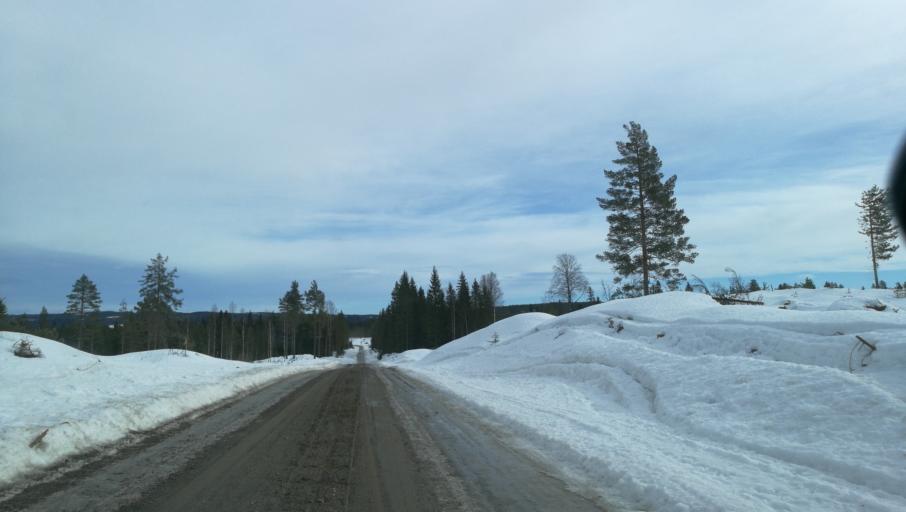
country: SE
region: Vaermland
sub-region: Torsby Kommun
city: Torsby
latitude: 60.6701
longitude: 12.8502
